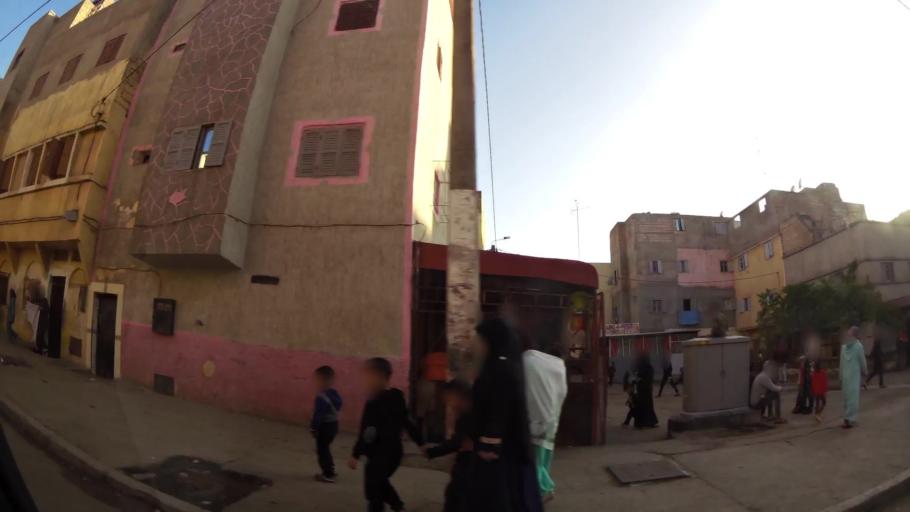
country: MA
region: Chaouia-Ouardigha
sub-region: Settat Province
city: Settat
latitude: 32.9981
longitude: -7.6081
